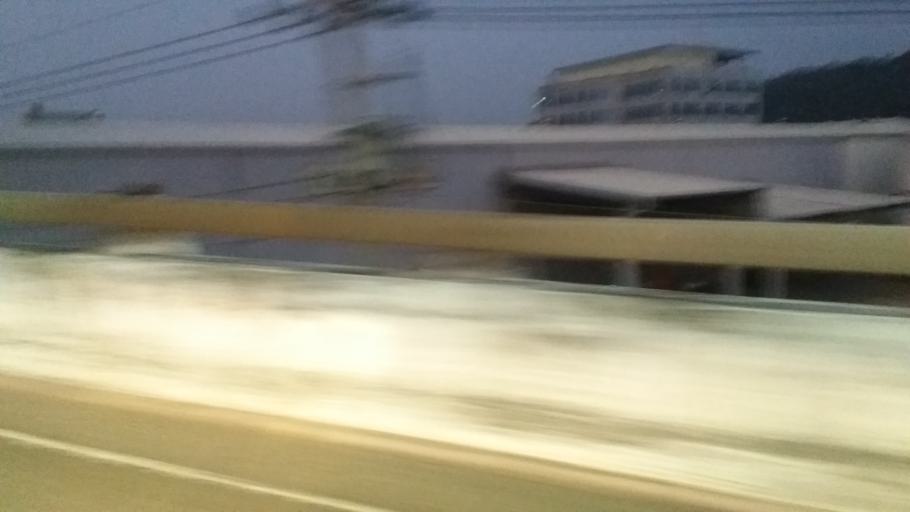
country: TW
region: Taiwan
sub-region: Hsinchu
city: Hsinchu
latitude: 24.7546
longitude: 120.9109
